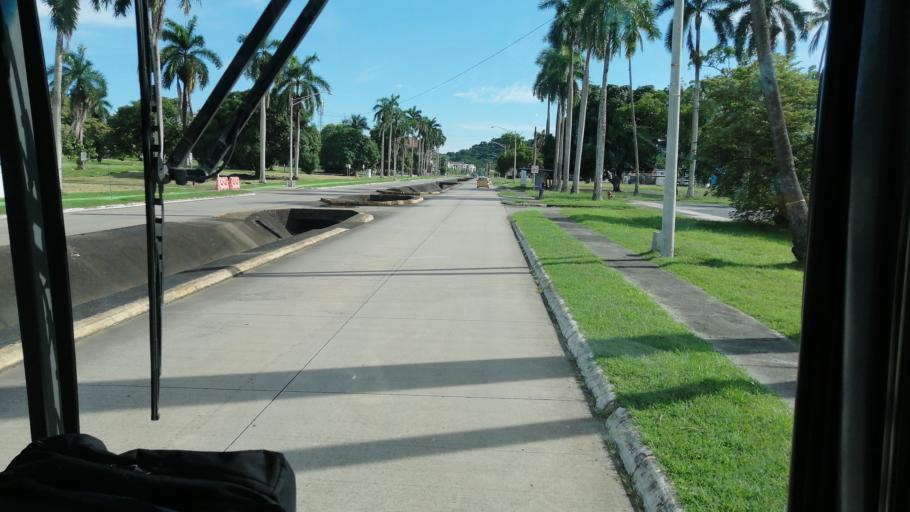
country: PA
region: Panama
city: Veracruz
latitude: 8.9142
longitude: -79.5920
